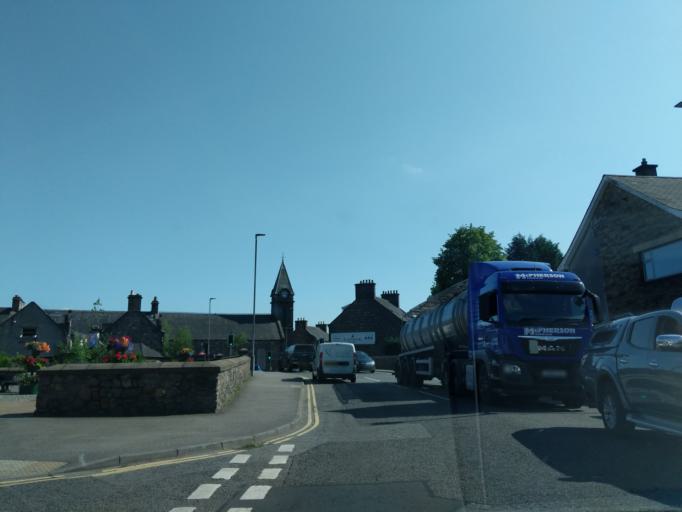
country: GB
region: Scotland
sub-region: Moray
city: Rothes
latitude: 57.5277
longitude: -3.2082
